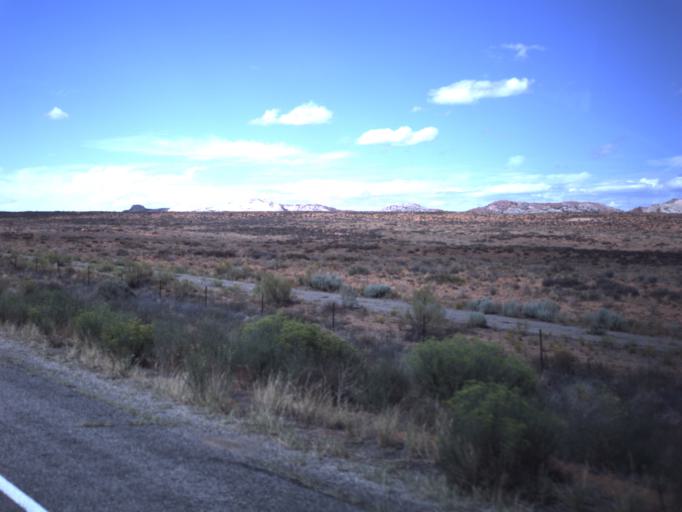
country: US
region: Utah
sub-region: San Juan County
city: Blanding
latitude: 37.2654
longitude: -109.6274
